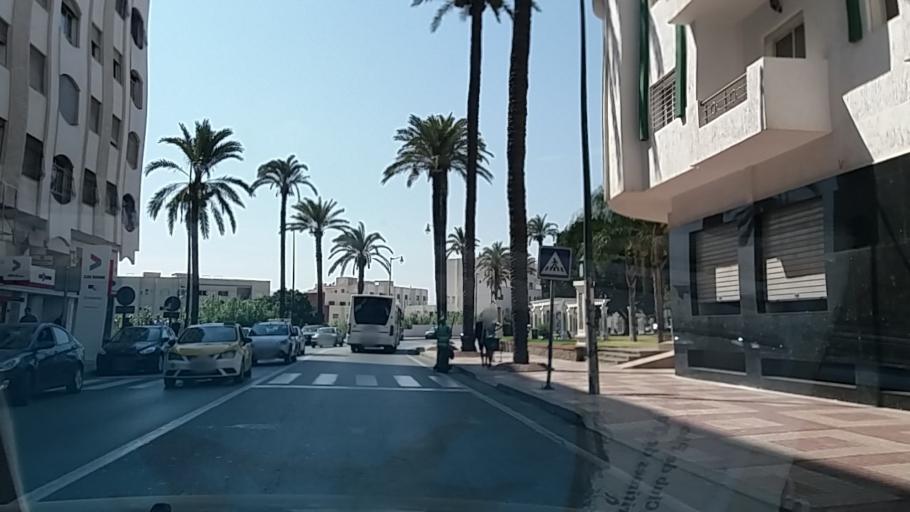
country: MA
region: Tanger-Tetouan
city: Tetouan
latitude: 35.5682
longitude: -5.3770
